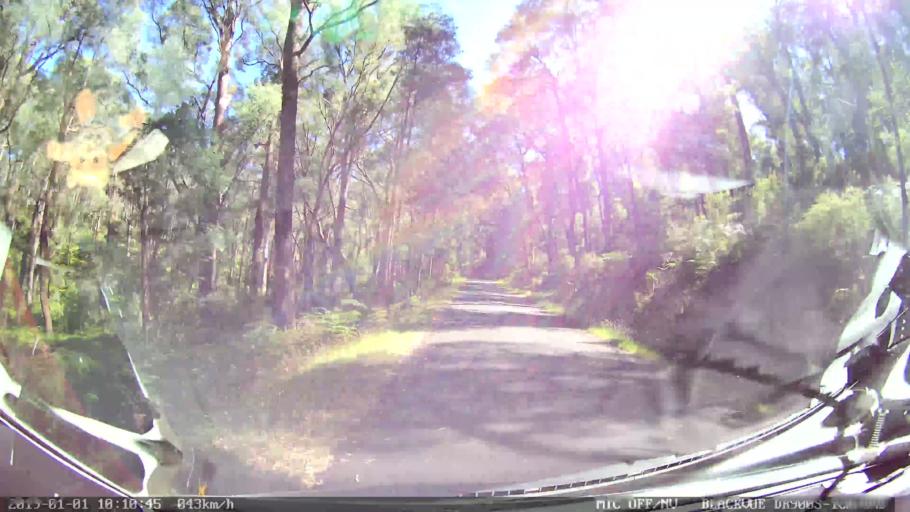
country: AU
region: New South Wales
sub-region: Snowy River
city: Jindabyne
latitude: -36.1391
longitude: 148.1580
